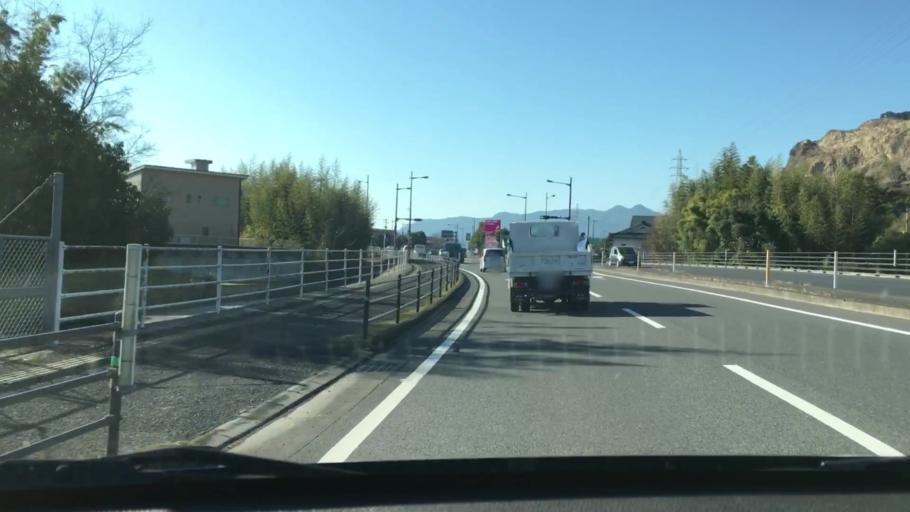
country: JP
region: Kagoshima
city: Kajiki
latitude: 31.7415
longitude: 130.6526
